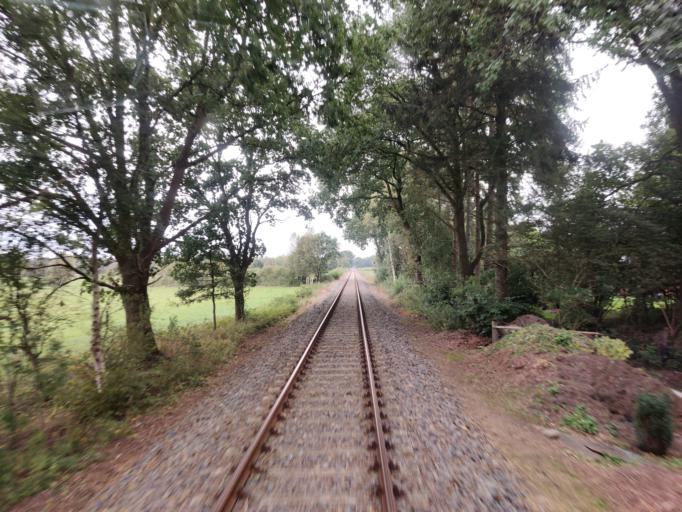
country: DE
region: Lower Saxony
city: Gnarrenburg
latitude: 53.3544
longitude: 9.0064
